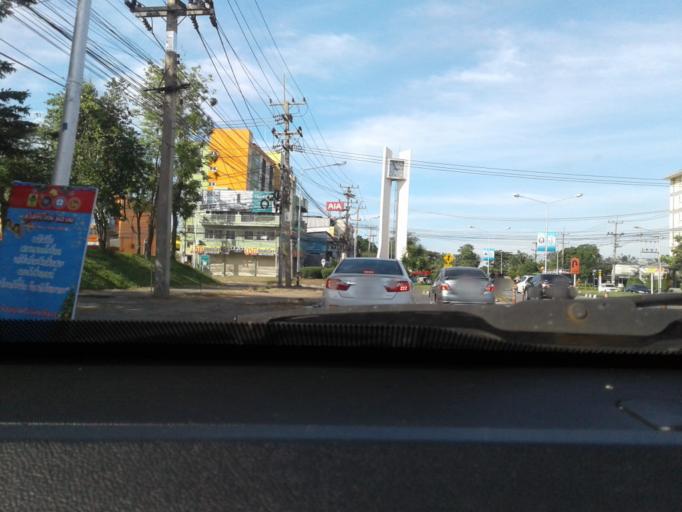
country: TH
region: Nakhon Pathom
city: Salaya
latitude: 13.8005
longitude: 100.3270
